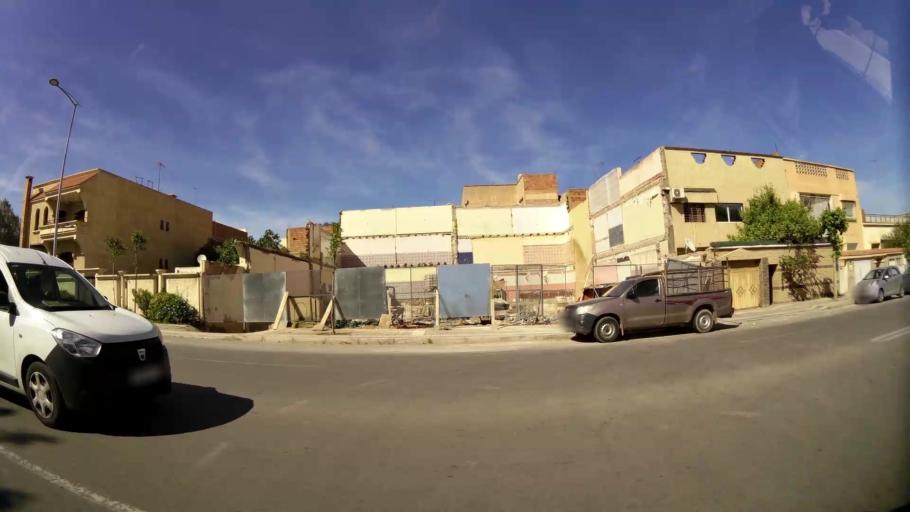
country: MA
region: Oriental
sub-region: Oujda-Angad
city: Oujda
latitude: 34.6660
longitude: -1.9148
